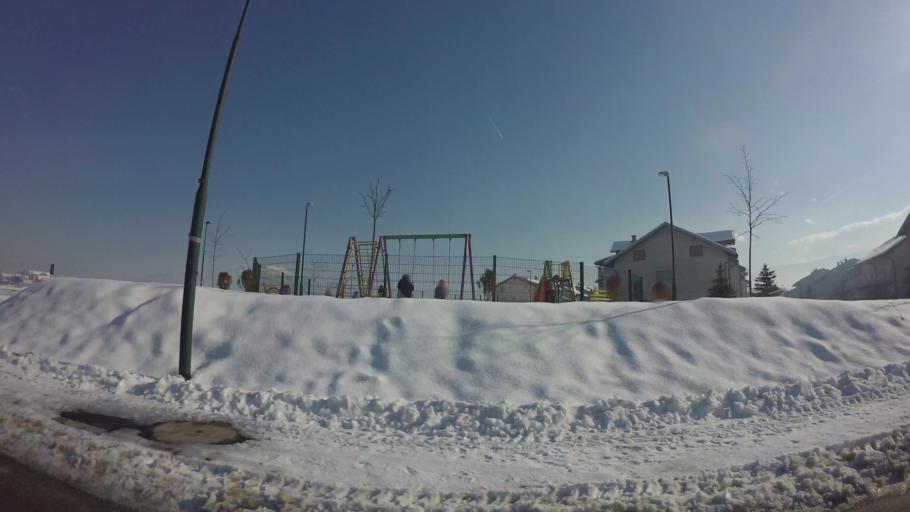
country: BA
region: Federation of Bosnia and Herzegovina
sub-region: Kanton Sarajevo
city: Sarajevo
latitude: 43.8182
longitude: 18.3135
